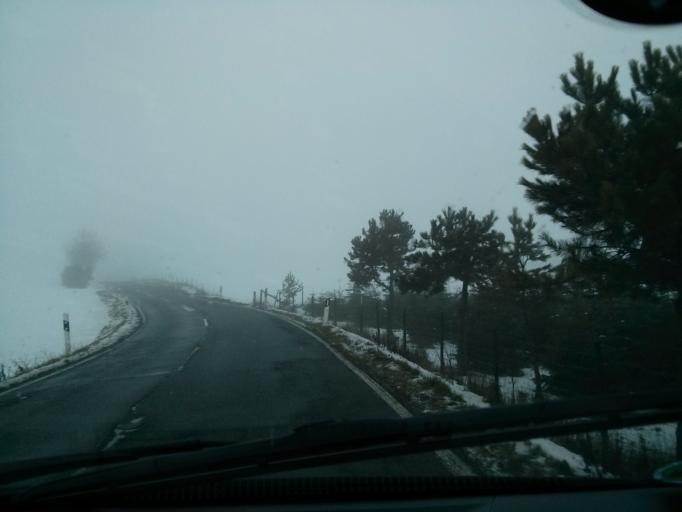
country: DE
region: Rheinland-Pfalz
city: Berg
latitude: 50.5704
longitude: 6.9501
